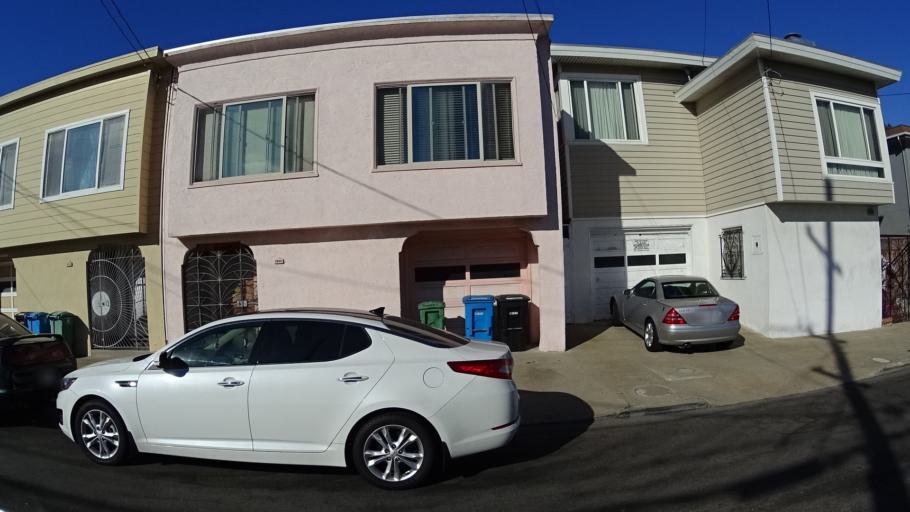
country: US
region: California
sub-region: San Mateo County
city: Brisbane
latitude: 37.7183
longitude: -122.4058
